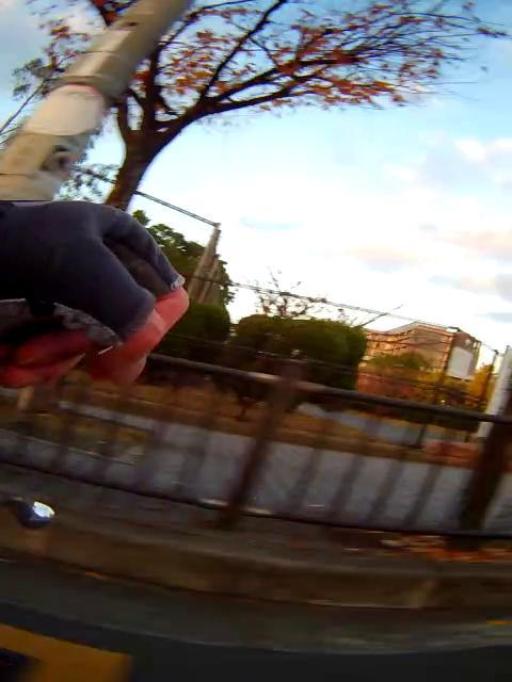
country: JP
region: Osaka
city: Suita
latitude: 34.7283
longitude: 135.5100
